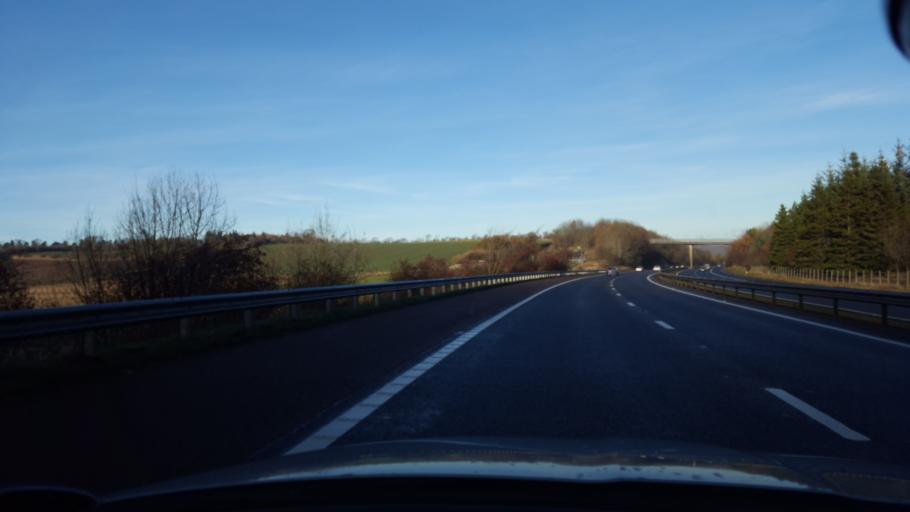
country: GB
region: Scotland
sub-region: Perth and Kinross
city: Bridge of Earn
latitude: 56.3237
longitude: -3.3959
